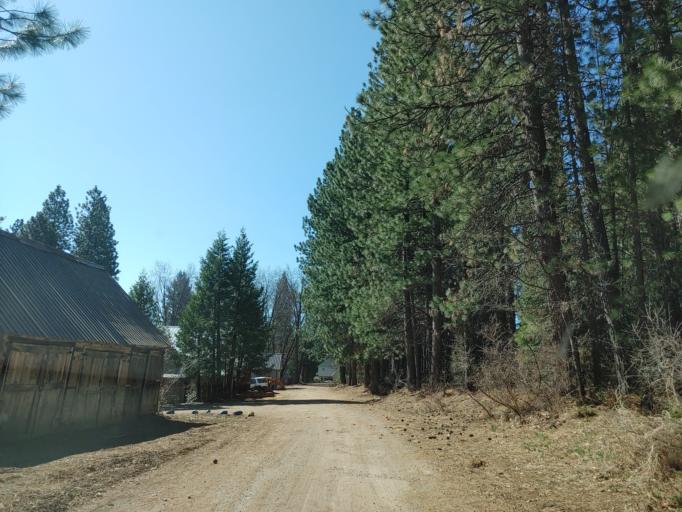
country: US
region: California
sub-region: Siskiyou County
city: McCloud
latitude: 41.2594
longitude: -122.1426
